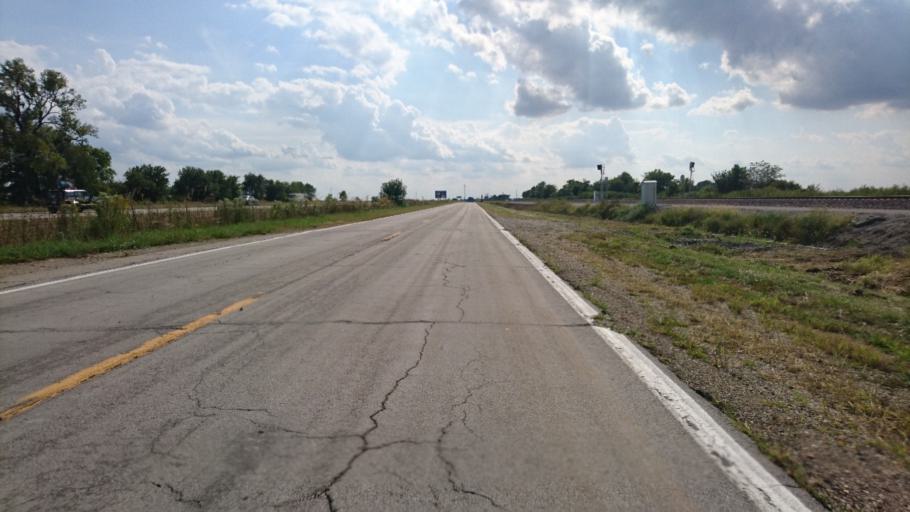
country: US
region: Illinois
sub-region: Logan County
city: Atlanta
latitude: 40.3378
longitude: -89.1421
